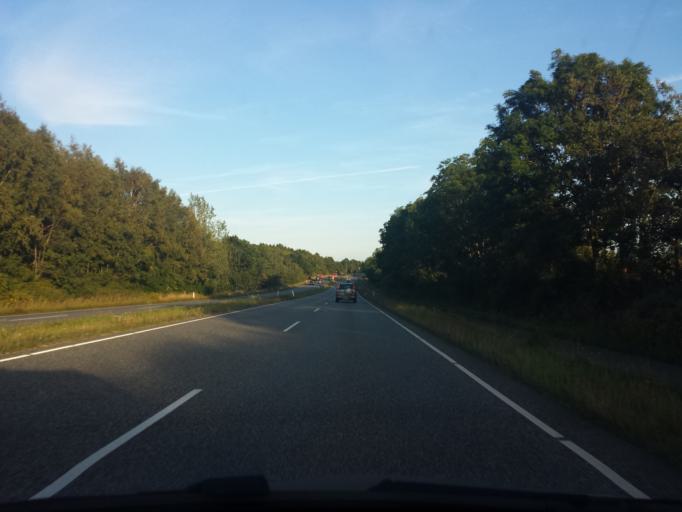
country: DK
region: Capital Region
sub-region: Egedal Kommune
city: Vekso
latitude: 55.7610
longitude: 12.2252
